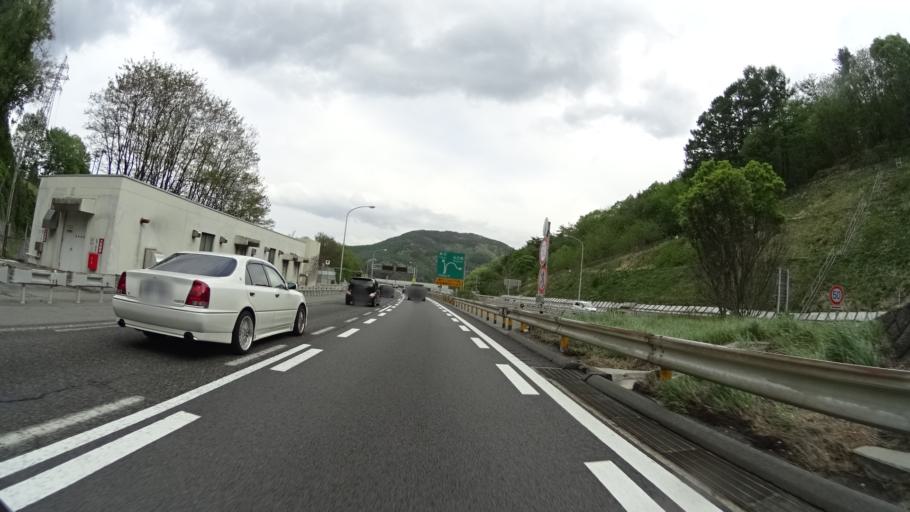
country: JP
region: Nagano
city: Okaya
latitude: 36.0696
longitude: 138.0366
